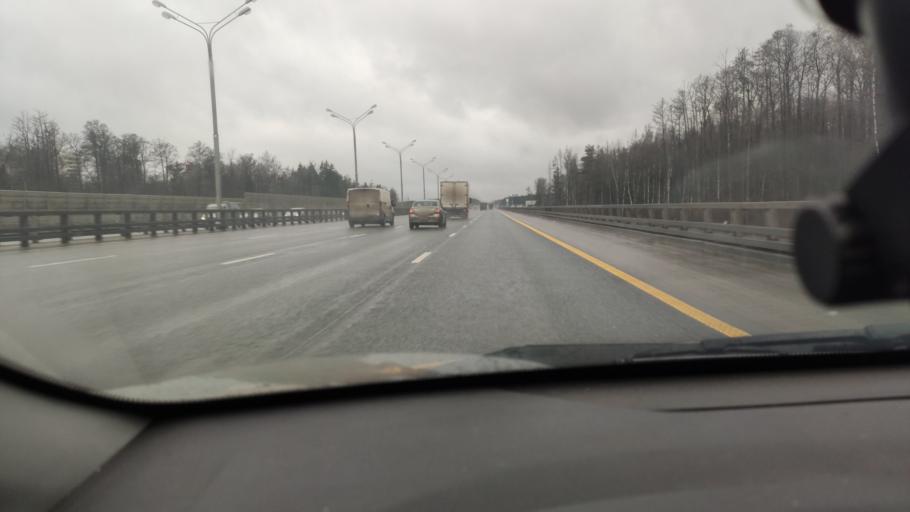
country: RU
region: Moskovskaya
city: Krasnoznamensk
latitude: 55.6076
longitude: 37.0374
